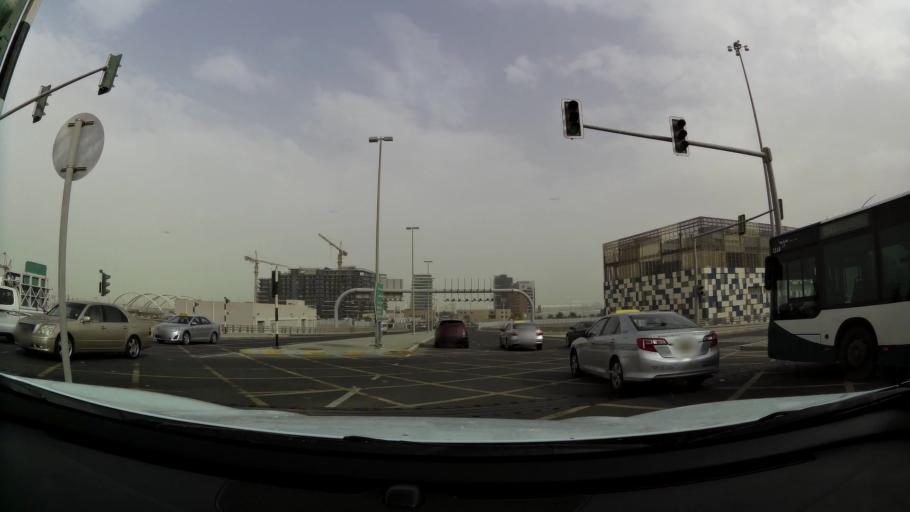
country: AE
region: Abu Dhabi
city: Abu Dhabi
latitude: 24.4458
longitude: 54.6010
